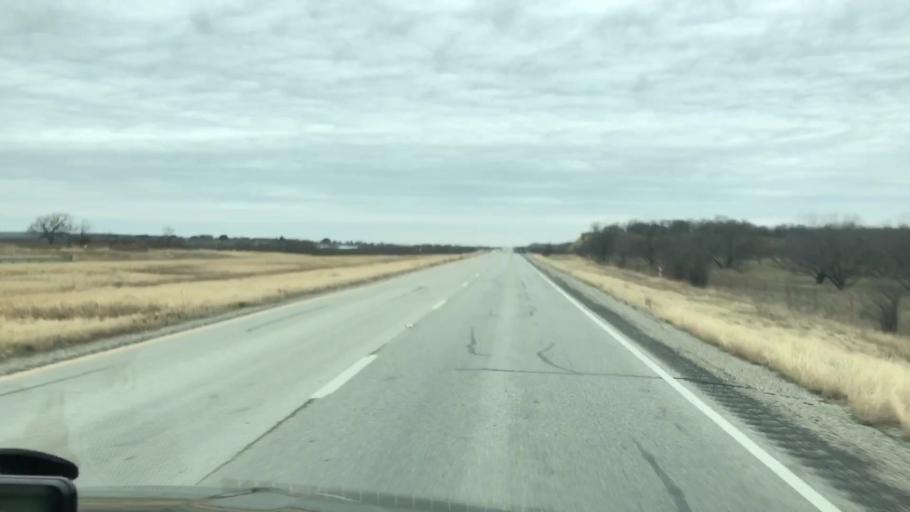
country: US
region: Texas
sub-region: Jack County
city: Jacksboro
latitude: 33.2369
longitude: -98.2088
